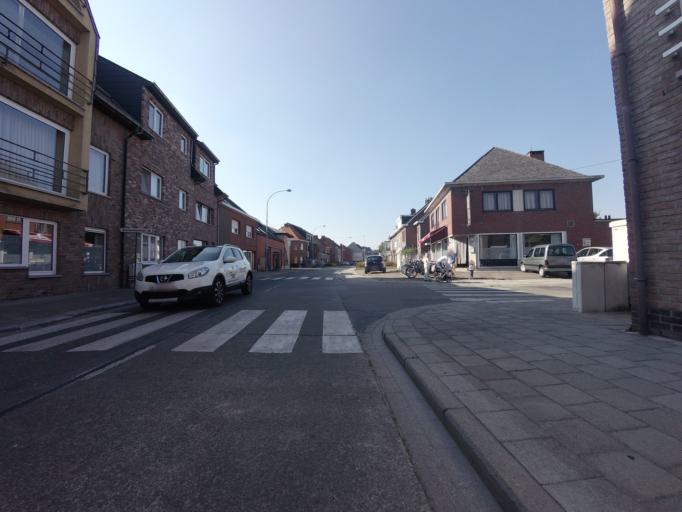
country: BE
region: Flanders
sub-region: Provincie Antwerpen
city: Willebroek
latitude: 51.0772
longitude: 4.3345
